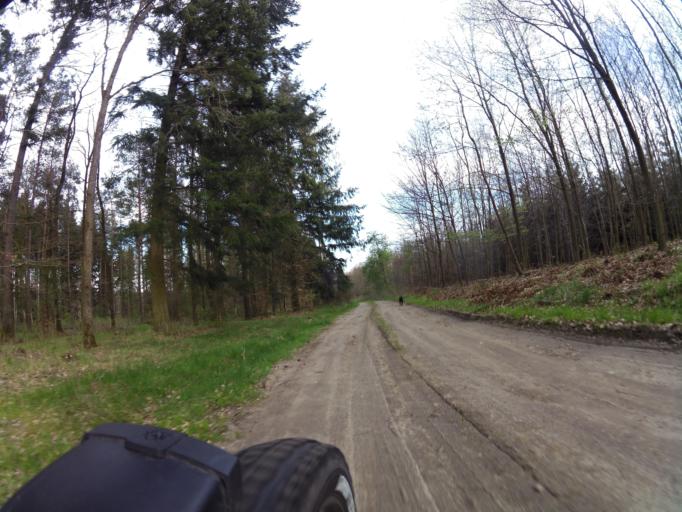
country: PL
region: West Pomeranian Voivodeship
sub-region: Powiat lobeski
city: Lobez
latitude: 53.7417
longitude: 15.6287
